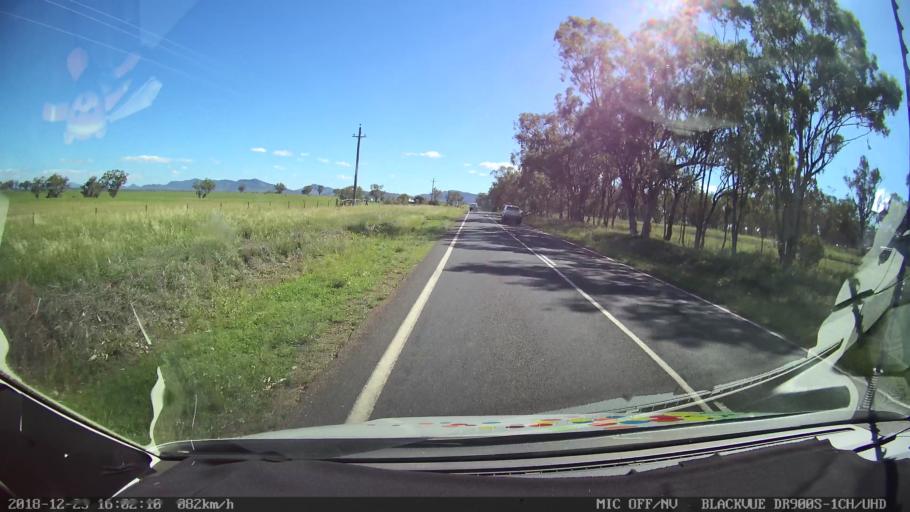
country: AU
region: New South Wales
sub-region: Tamworth Municipality
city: Phillip
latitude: -31.2294
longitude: 150.8112
